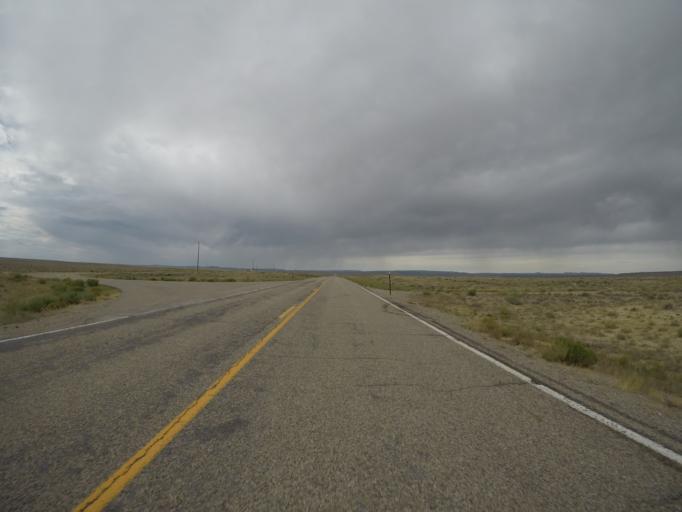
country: US
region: Wyoming
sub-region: Lincoln County
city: Kemmerer
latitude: 41.9630
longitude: -110.1261
